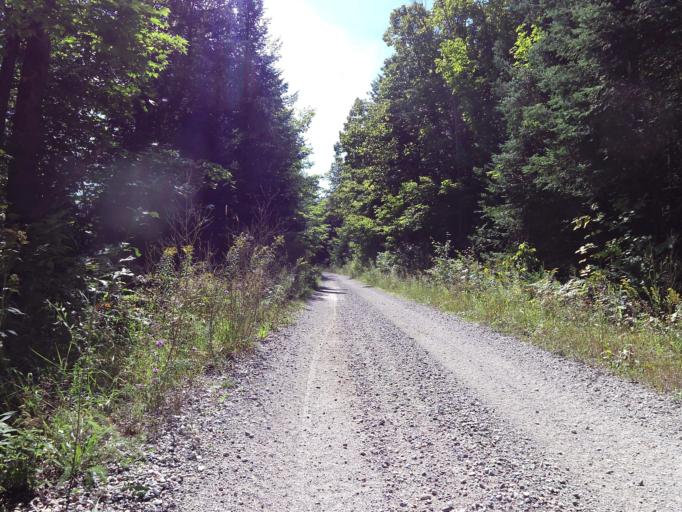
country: CA
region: Ontario
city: Renfrew
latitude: 45.0347
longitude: -76.7052
